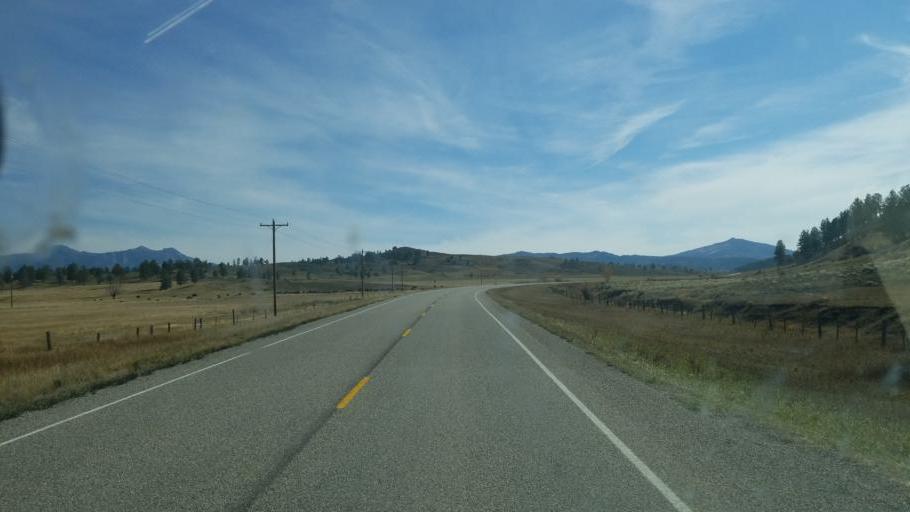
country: US
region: New Mexico
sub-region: Rio Arriba County
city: Dulce
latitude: 37.0334
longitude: -106.8342
